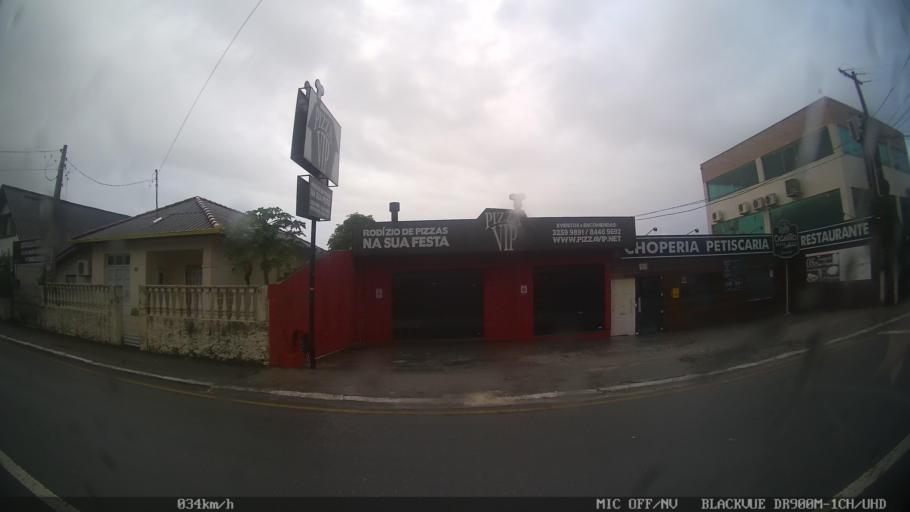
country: BR
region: Santa Catarina
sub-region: Sao Jose
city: Campinas
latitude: -27.6047
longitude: -48.6233
